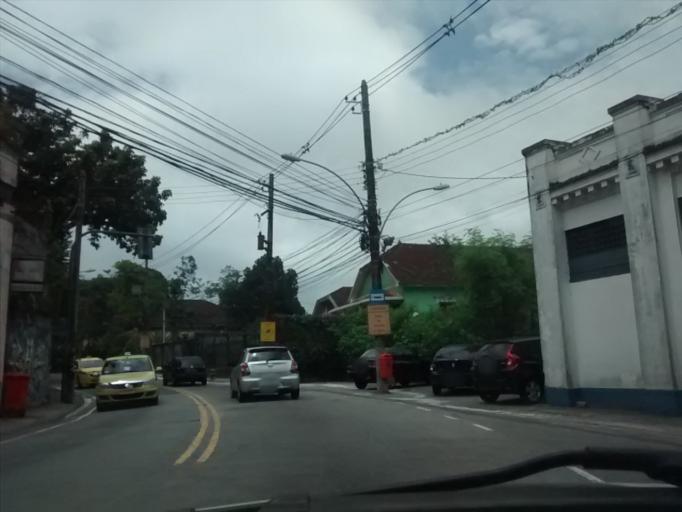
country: BR
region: Rio de Janeiro
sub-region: Rio De Janeiro
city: Rio de Janeiro
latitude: -22.9642
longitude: -43.2767
